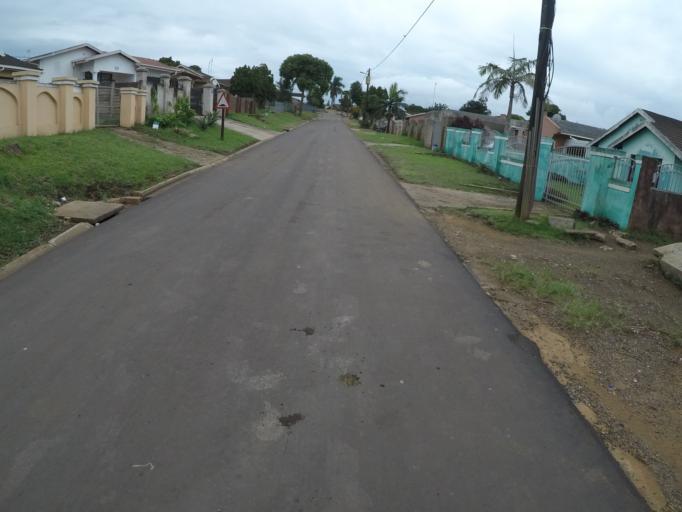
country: ZA
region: KwaZulu-Natal
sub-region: uThungulu District Municipality
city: Empangeni
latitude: -28.7757
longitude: 31.8530
